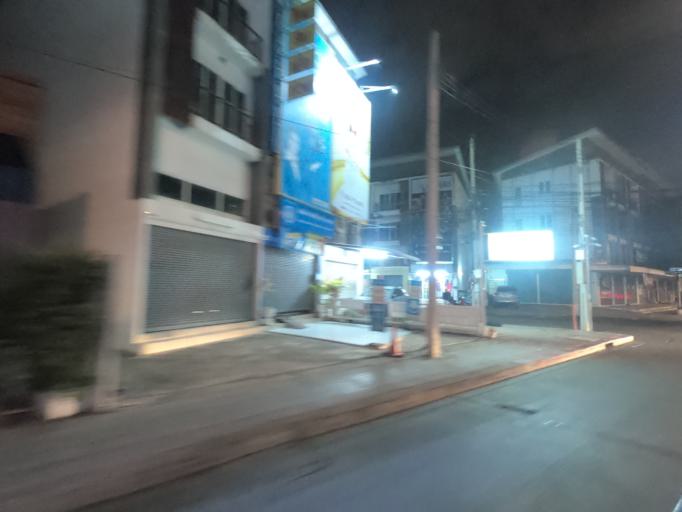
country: TH
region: Bangkok
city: Lat Phrao
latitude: 13.8056
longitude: 100.6076
